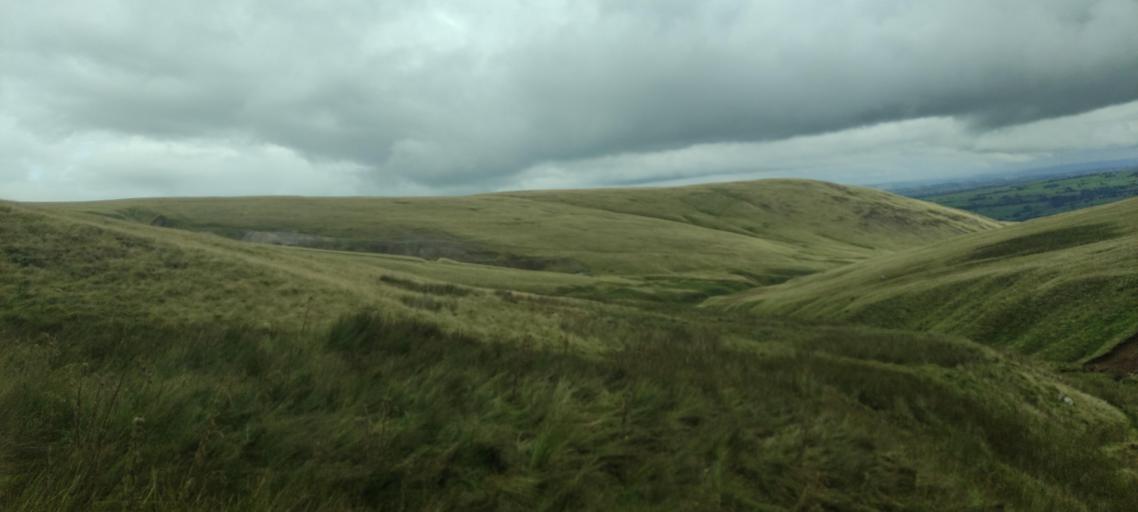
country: GB
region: England
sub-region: Cumbria
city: Keswick
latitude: 54.7022
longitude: -3.0491
